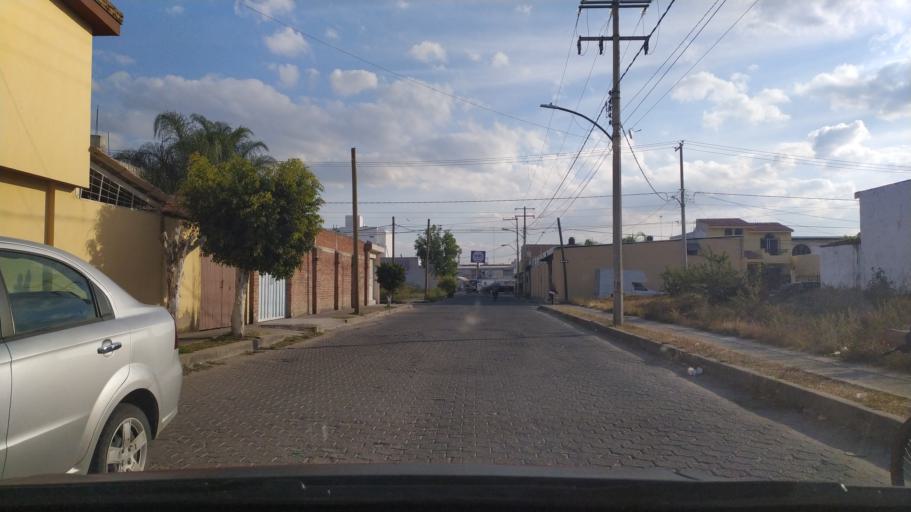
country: MX
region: Guanajuato
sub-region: Purisima del Rincon
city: Monte Grande
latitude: 21.0072
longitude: -101.8602
